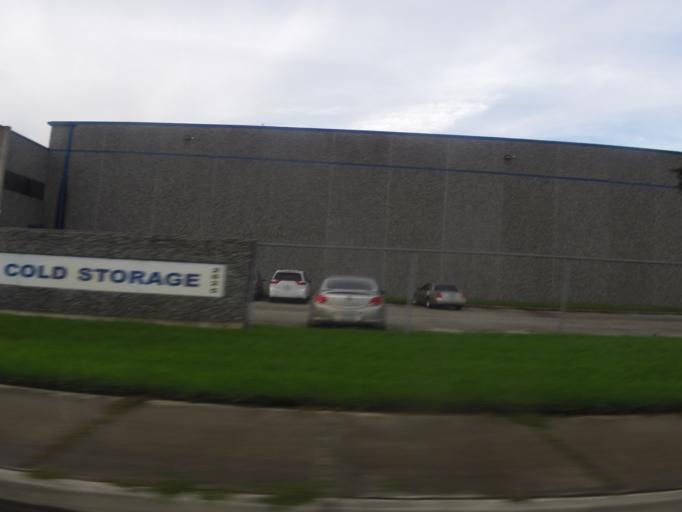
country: US
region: Florida
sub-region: Duval County
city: Jacksonville
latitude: 30.3440
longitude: -81.7092
